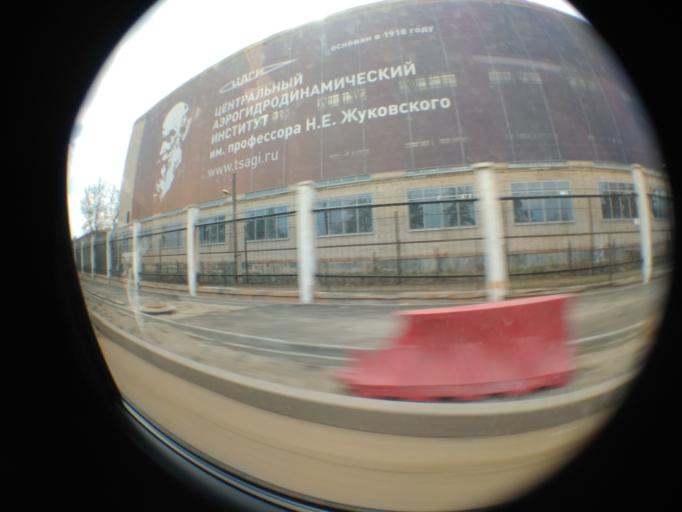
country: RU
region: Moskovskaya
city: Zhukovskiy
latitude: 55.5910
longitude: 38.1170
